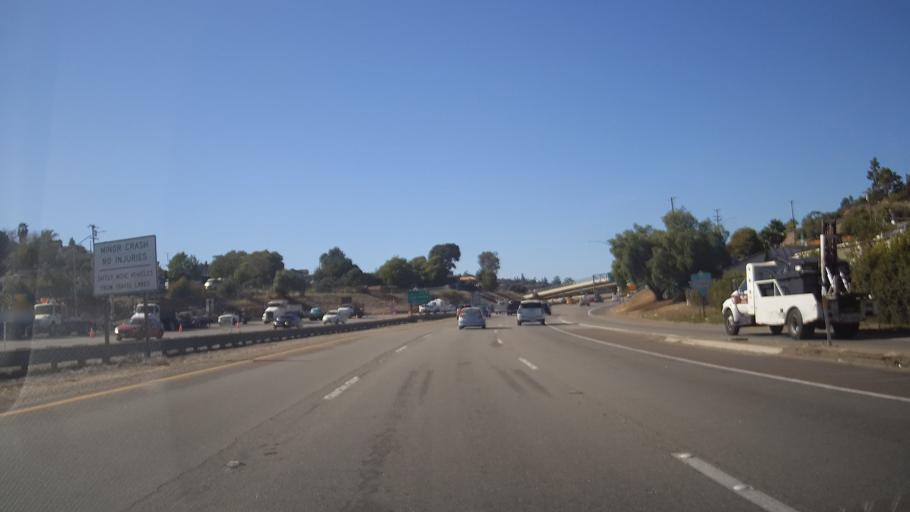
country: US
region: California
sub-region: San Diego County
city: Spring Valley
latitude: 32.7510
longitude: -117.0030
